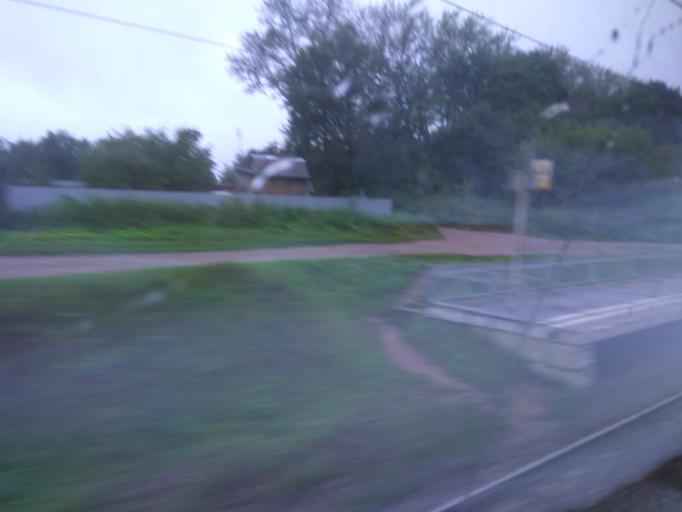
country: RU
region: Moskovskaya
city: Ozherel'ye
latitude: 54.8298
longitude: 38.2448
